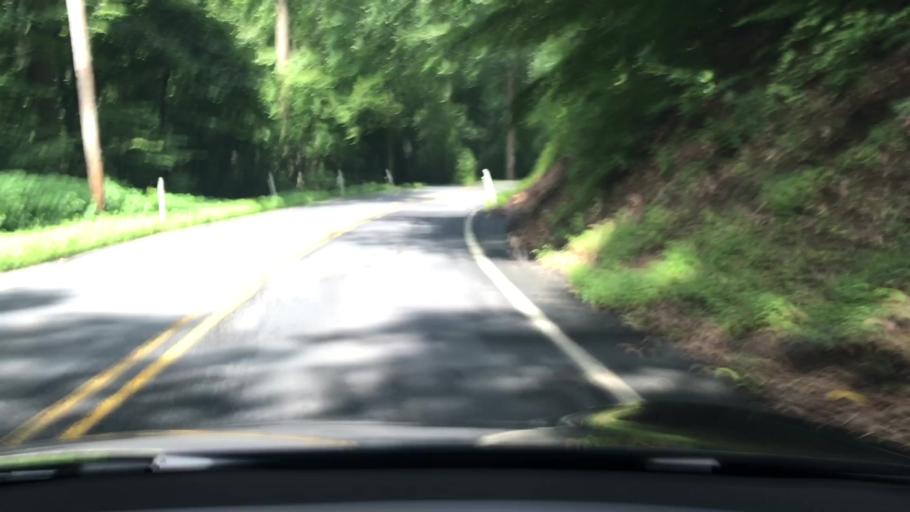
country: US
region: Pennsylvania
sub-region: Cumberland County
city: New Cumberland
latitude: 40.1910
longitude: -76.8741
